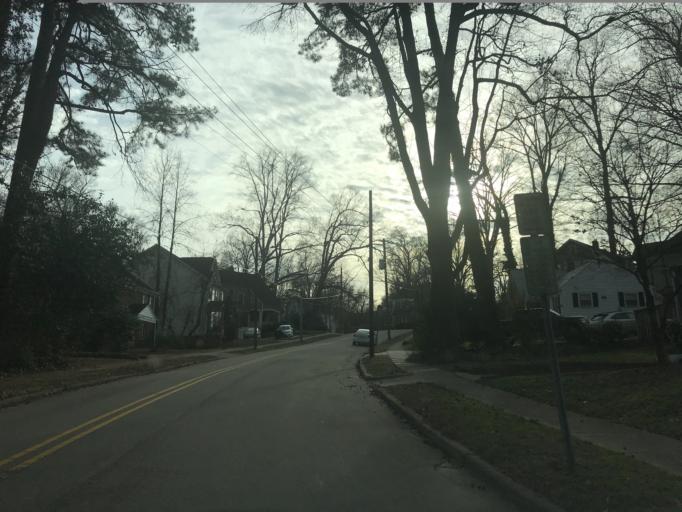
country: US
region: North Carolina
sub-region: Wake County
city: West Raleigh
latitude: 35.7947
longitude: -78.6695
